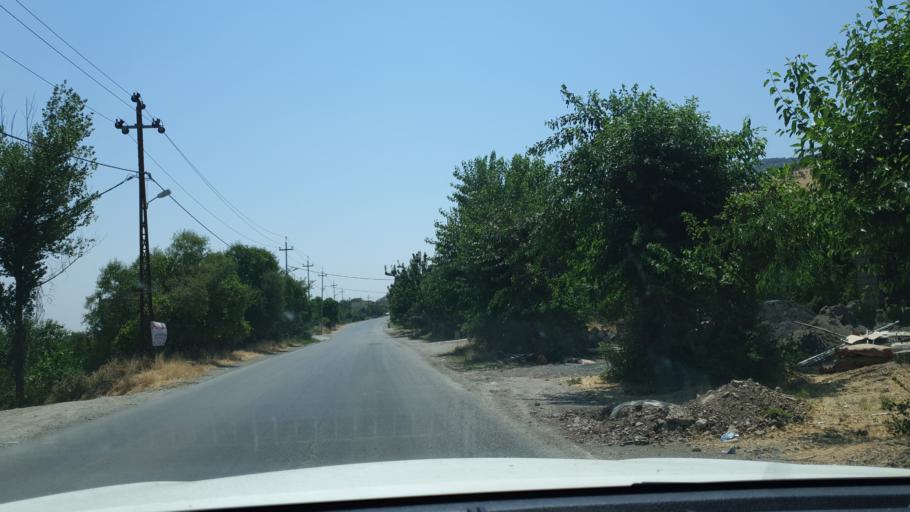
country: IQ
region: Arbil
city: Nahiyat Hiran
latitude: 36.2976
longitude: 44.4723
